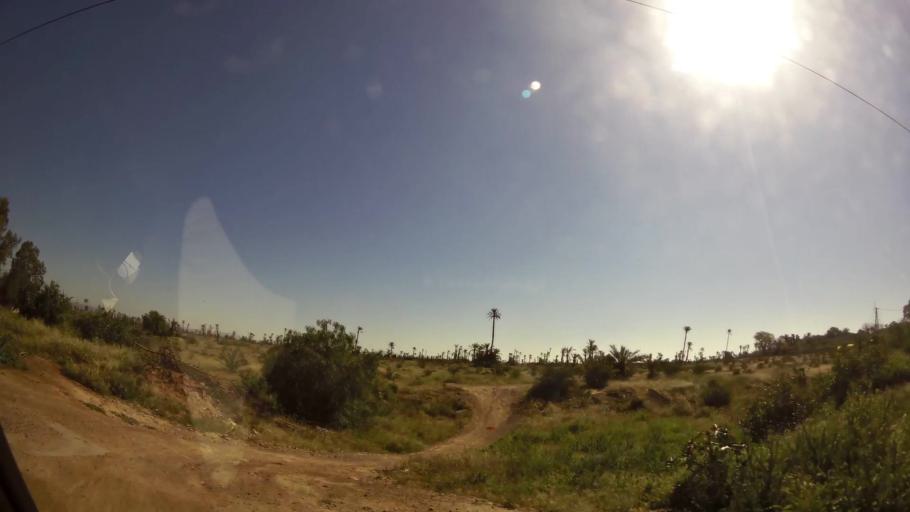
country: MA
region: Marrakech-Tensift-Al Haouz
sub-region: Marrakech
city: Marrakesh
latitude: 31.6629
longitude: -7.9353
